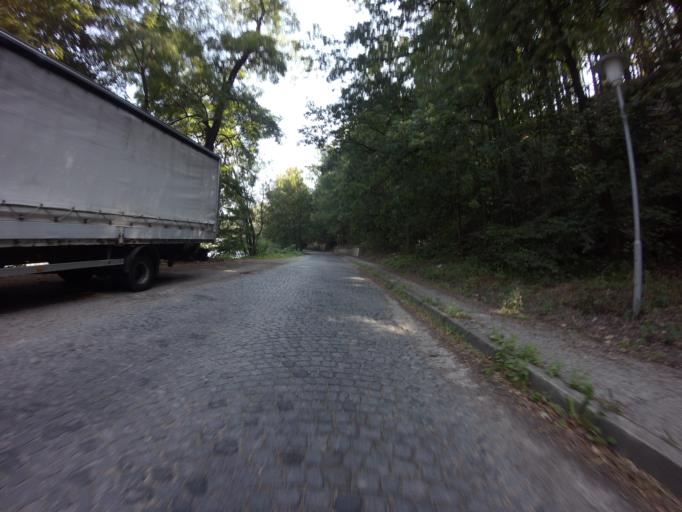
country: CZ
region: Jihocesky
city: Vcelna
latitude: 48.9175
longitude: 14.4315
